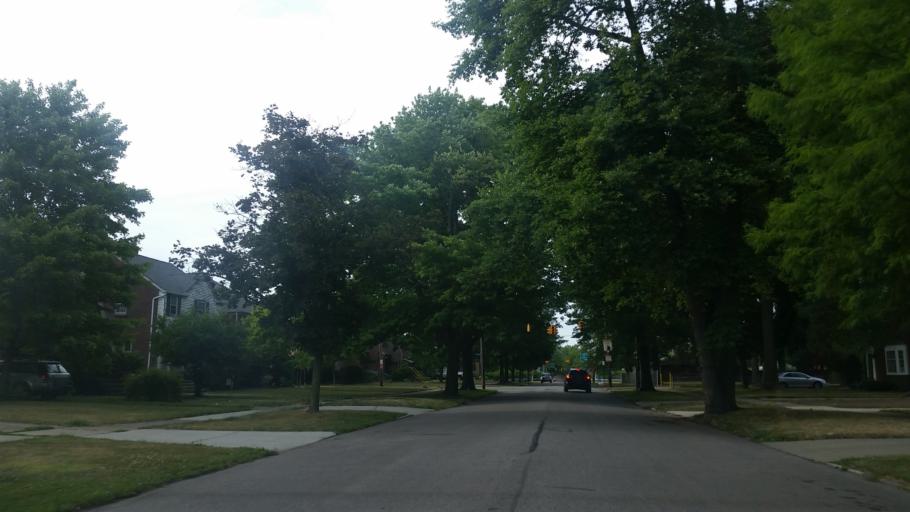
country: US
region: Ohio
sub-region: Cuyahoga County
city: Lakewood
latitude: 41.4672
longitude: -81.8089
